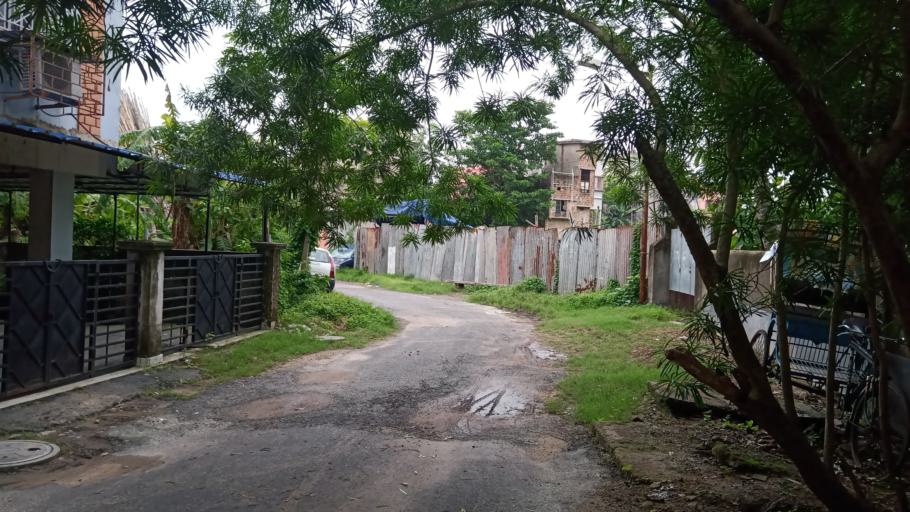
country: IN
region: West Bengal
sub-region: Kolkata
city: Kolkata
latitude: 22.4675
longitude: 88.3883
